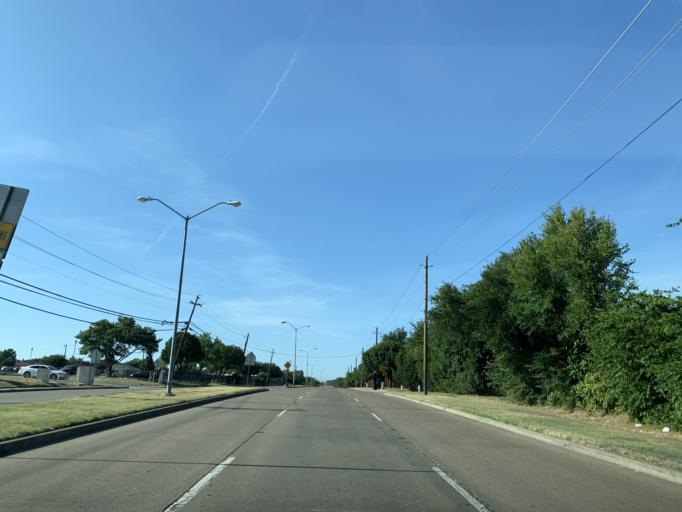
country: US
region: Texas
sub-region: Dallas County
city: Cockrell Hill
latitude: 32.7065
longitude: -96.8913
